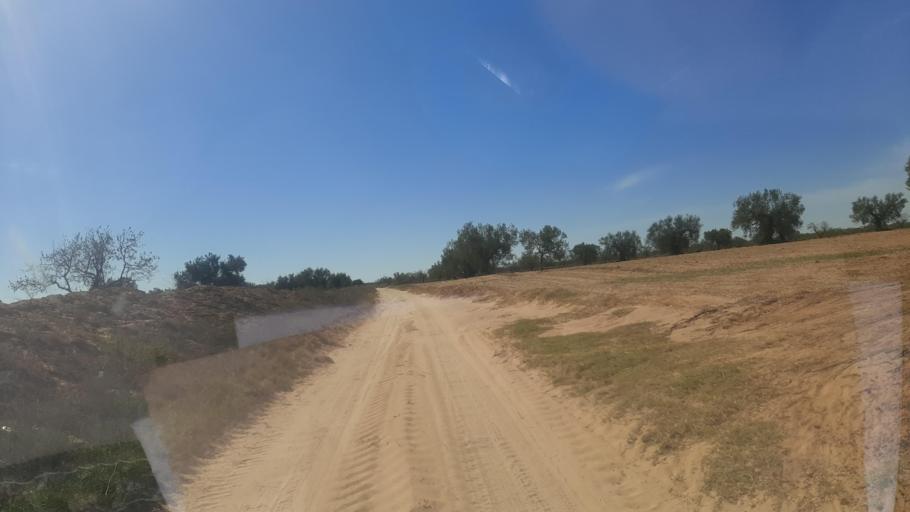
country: TN
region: Safaqis
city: Sfax
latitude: 34.8244
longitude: 10.5535
